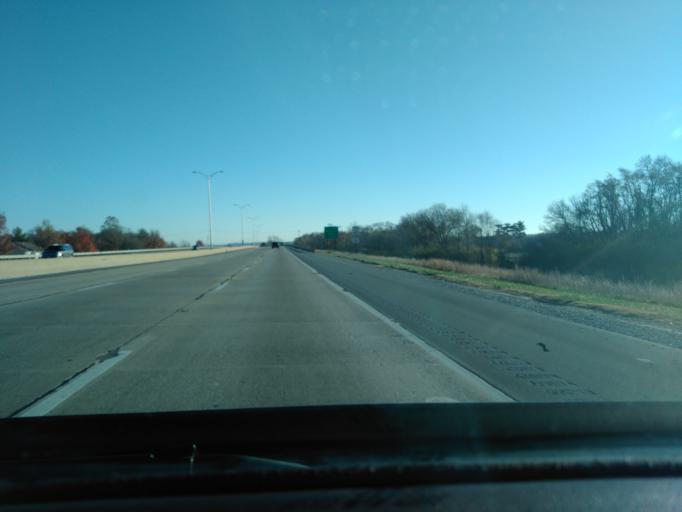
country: US
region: Illinois
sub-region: Saint Clair County
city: Centreville
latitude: 38.5560
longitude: -90.1523
